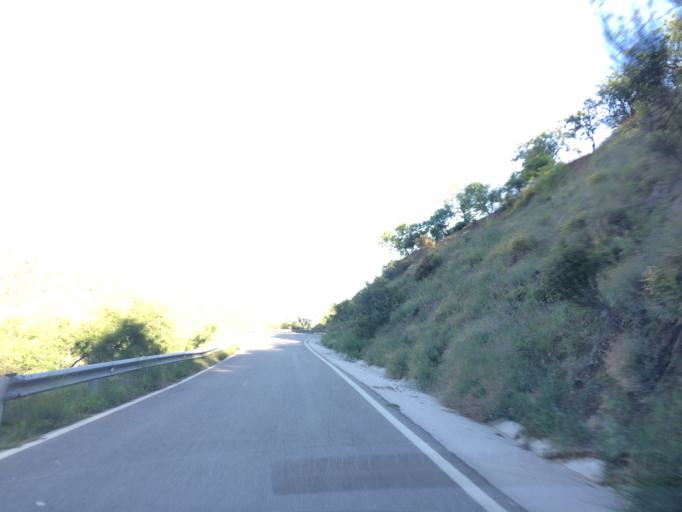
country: ES
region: Andalusia
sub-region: Provincia de Malaga
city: Totalan
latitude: 36.7807
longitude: -4.3202
